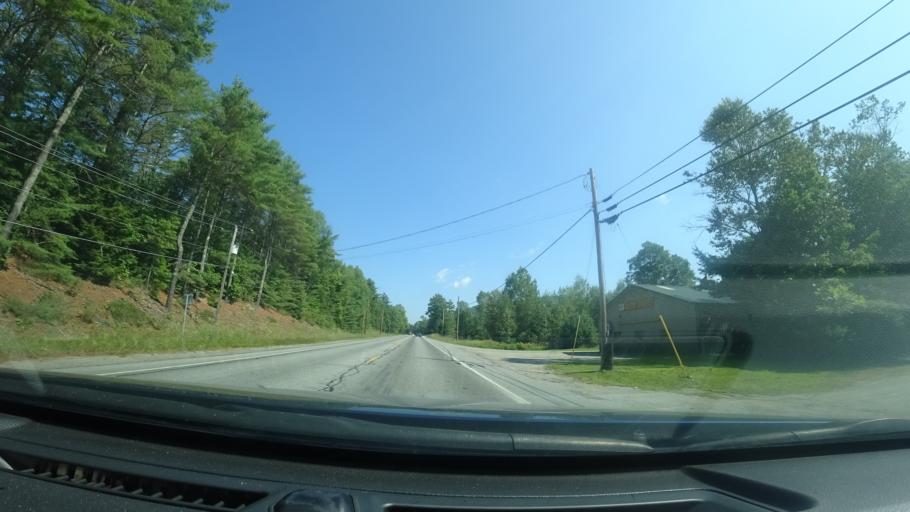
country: US
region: New York
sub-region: Warren County
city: Warrensburg
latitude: 43.6331
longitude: -73.7984
